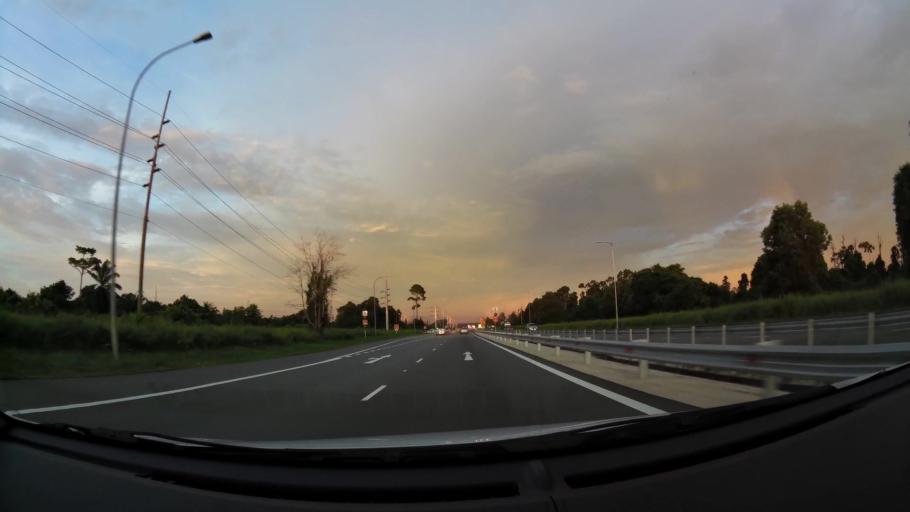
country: BN
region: Belait
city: Kuala Belait
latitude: 4.5799
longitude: 114.2578
